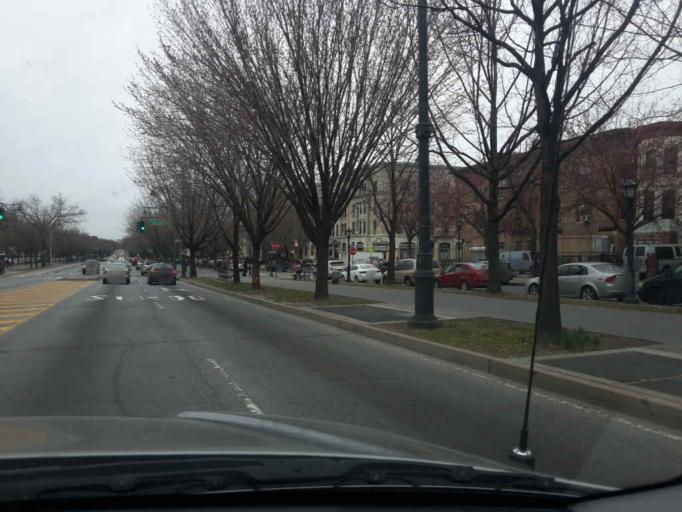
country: US
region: New York
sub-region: Kings County
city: Brooklyn
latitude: 40.6694
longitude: -73.9413
